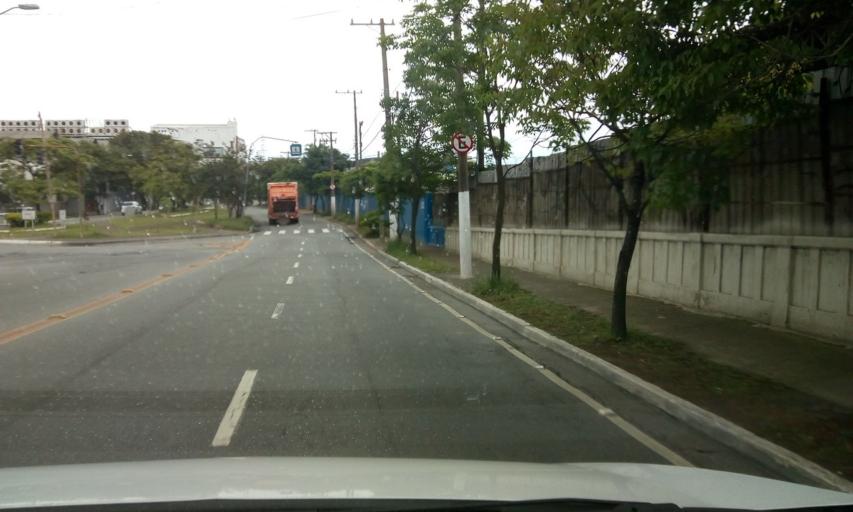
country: BR
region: Sao Paulo
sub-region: Sao Paulo
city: Sao Paulo
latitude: -23.5665
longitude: -46.6053
